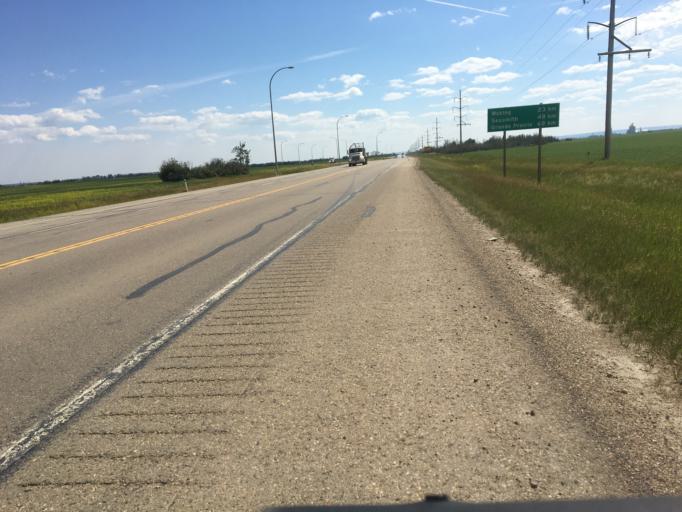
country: CA
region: Alberta
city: Spirit River
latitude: 55.7492
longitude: -118.6986
